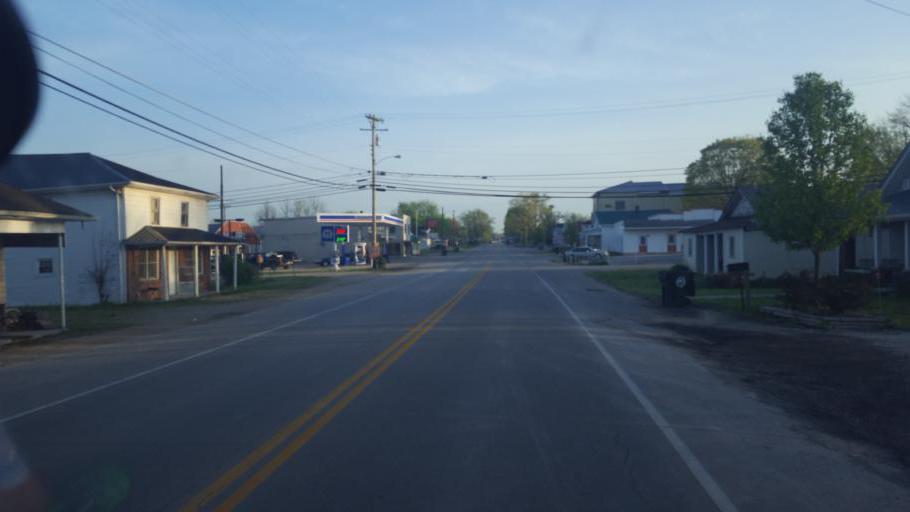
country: US
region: Kentucky
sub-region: Hart County
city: Munfordville
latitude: 37.3760
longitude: -85.9027
